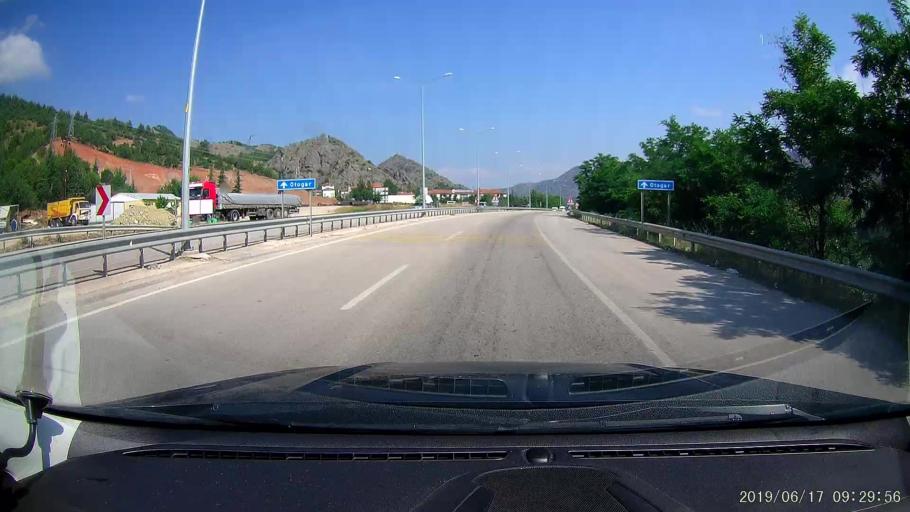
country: TR
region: Amasya
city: Amasya
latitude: 40.7006
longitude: 35.8066
